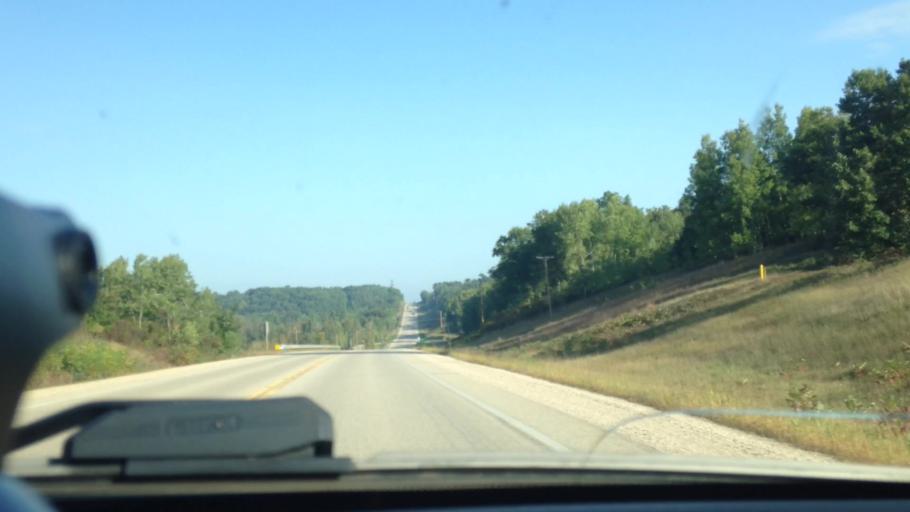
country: US
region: Wisconsin
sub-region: Marinette County
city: Niagara
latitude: 45.4051
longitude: -87.9706
